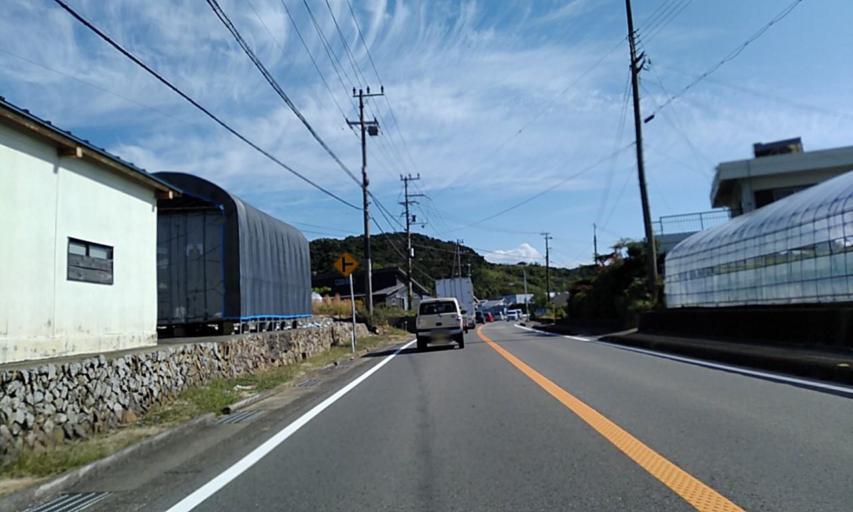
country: JP
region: Wakayama
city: Gobo
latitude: 33.8550
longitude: 135.1649
